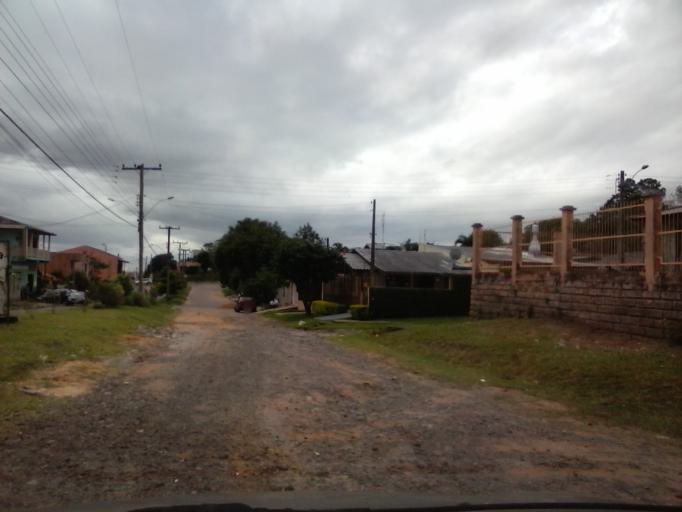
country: BR
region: Rio Grande do Sul
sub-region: Sapucaia Do Sul
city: Sapucaia
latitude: -29.8424
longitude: -51.1164
